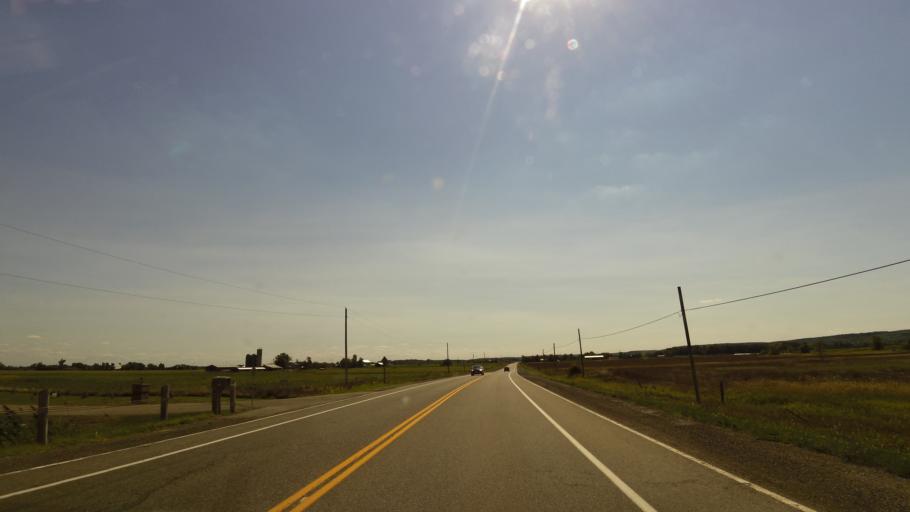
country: CA
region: Ontario
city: Brampton
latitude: 43.7580
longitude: -79.8951
